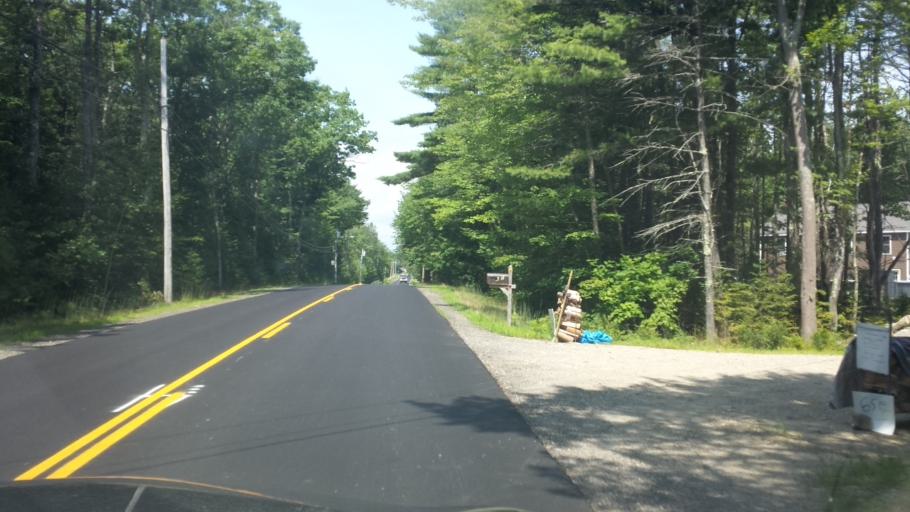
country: US
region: Maine
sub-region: York County
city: Biddeford
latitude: 43.4451
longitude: -70.4134
